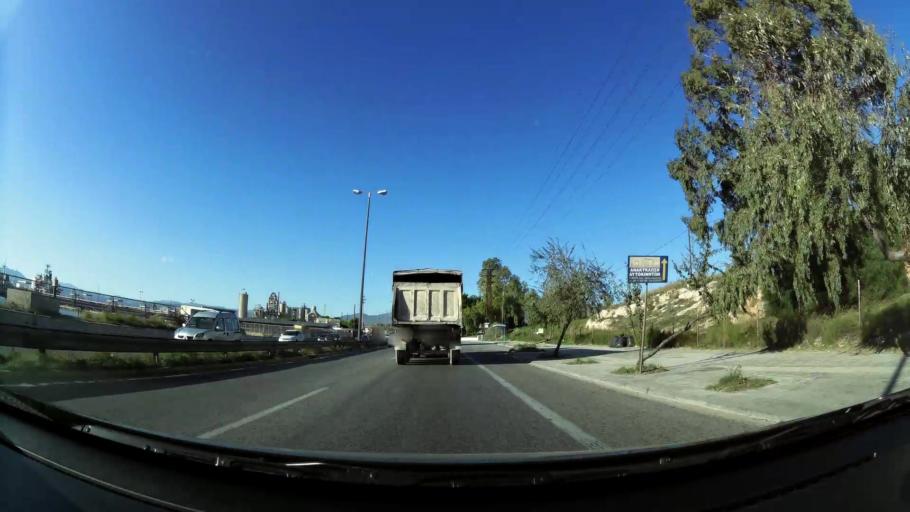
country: GR
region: Attica
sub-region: Nomarchia Athinas
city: Skaramangas
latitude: 38.0279
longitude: 23.5981
